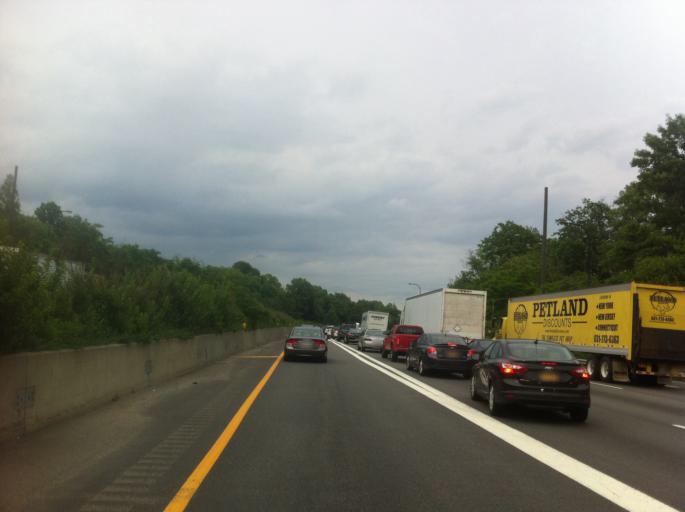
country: US
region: New York
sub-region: Nassau County
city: Lake Success
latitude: 40.7667
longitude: -73.7158
